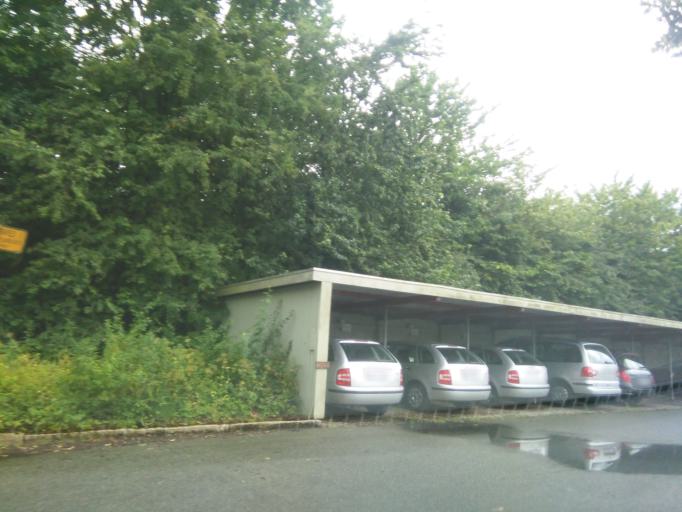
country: DK
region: Central Jutland
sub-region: Arhus Kommune
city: Arhus
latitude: 56.1093
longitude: 10.2046
